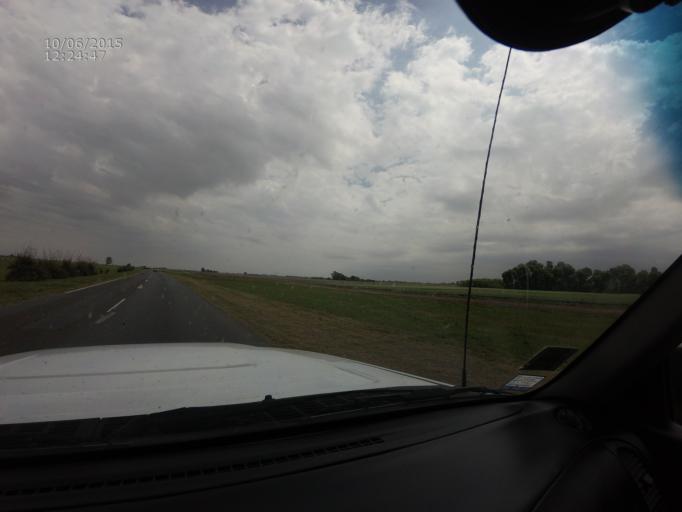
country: AR
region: Santa Fe
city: Roldan
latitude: -32.9090
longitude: -60.9845
